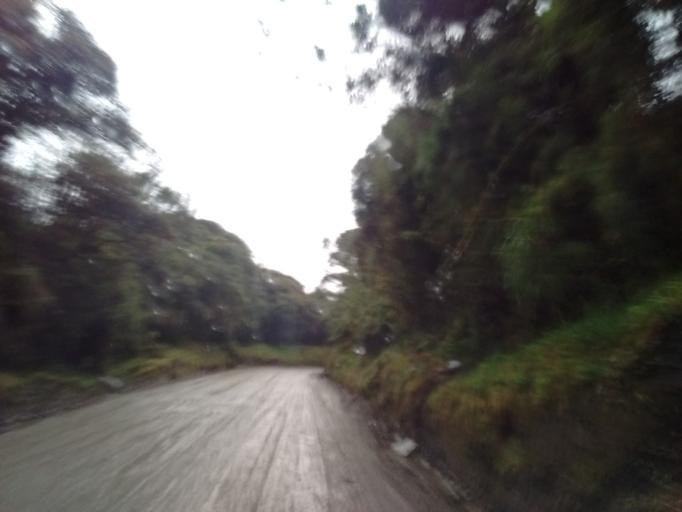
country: CO
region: Cauca
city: Paispamba
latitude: 2.1579
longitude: -76.4535
